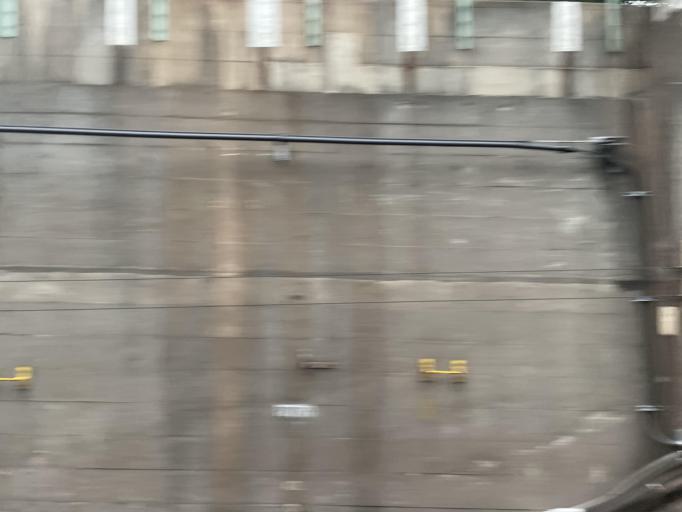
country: JP
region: Tokyo
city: Urayasu
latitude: 35.6674
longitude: 139.8350
